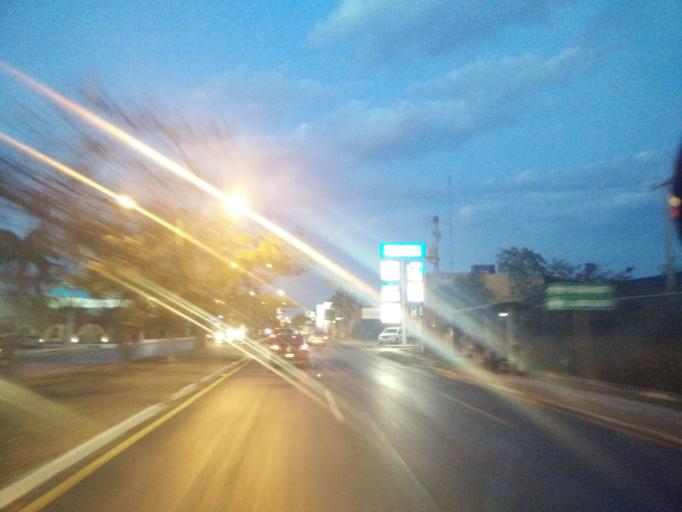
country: MX
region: Yucatan
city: Merida
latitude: 20.9474
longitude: -89.6519
